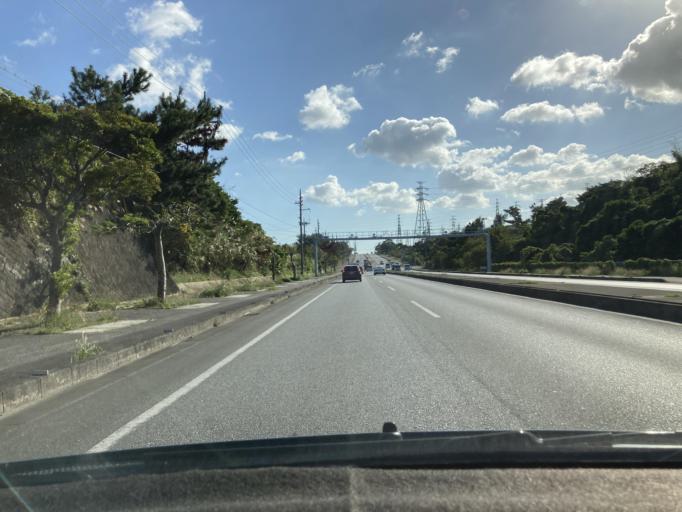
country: JP
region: Okinawa
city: Ishikawa
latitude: 26.3983
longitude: 127.8291
